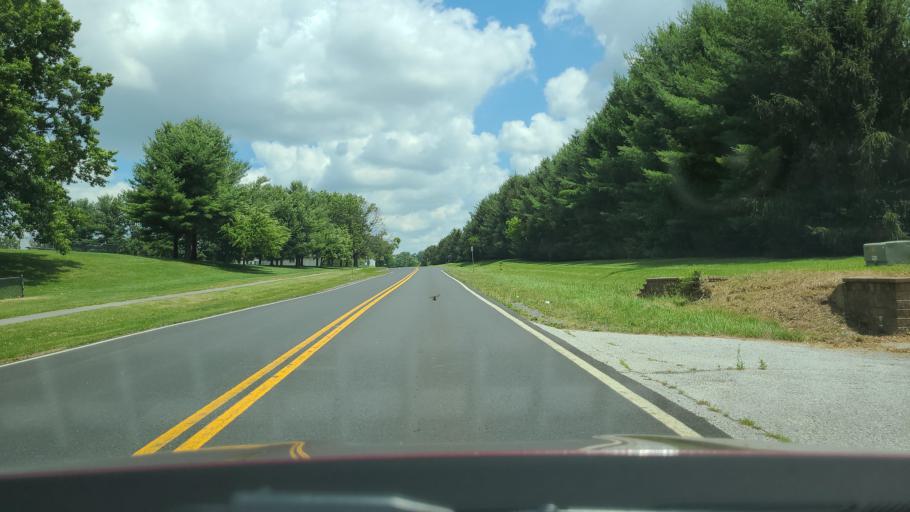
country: US
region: Maryland
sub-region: Carroll County
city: Westminster
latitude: 39.5444
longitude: -77.0025
